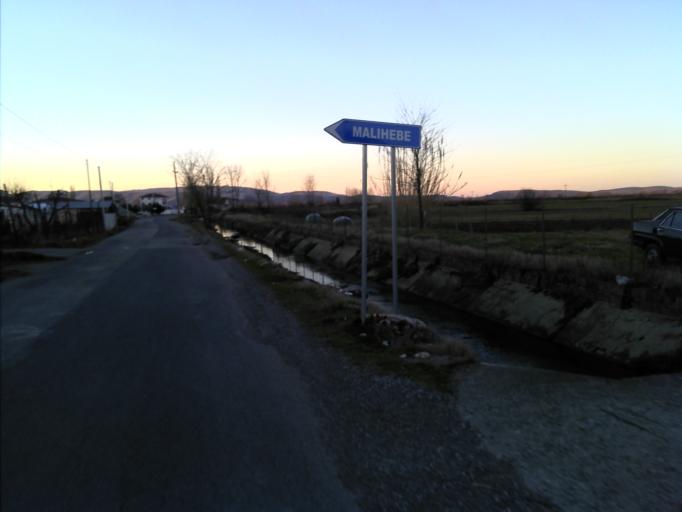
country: AL
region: Shkoder
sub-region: Rrethi i Shkodres
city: Berdica e Madhe
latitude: 42.0103
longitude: 19.4806
